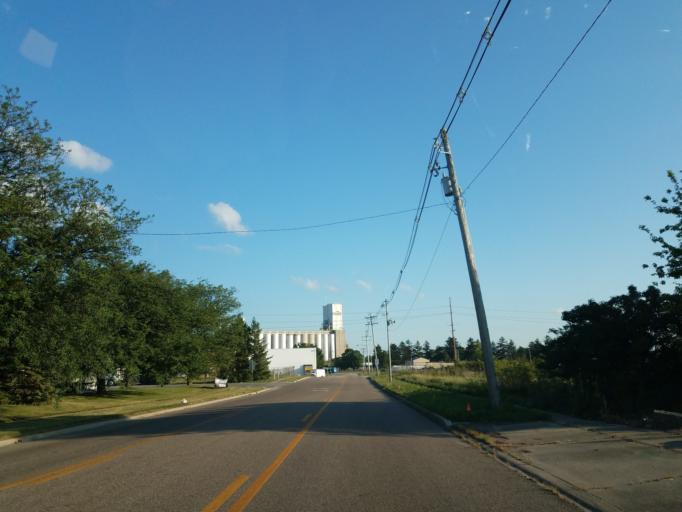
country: US
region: Illinois
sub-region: McLean County
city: Bloomington
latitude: 40.4817
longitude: -89.0184
